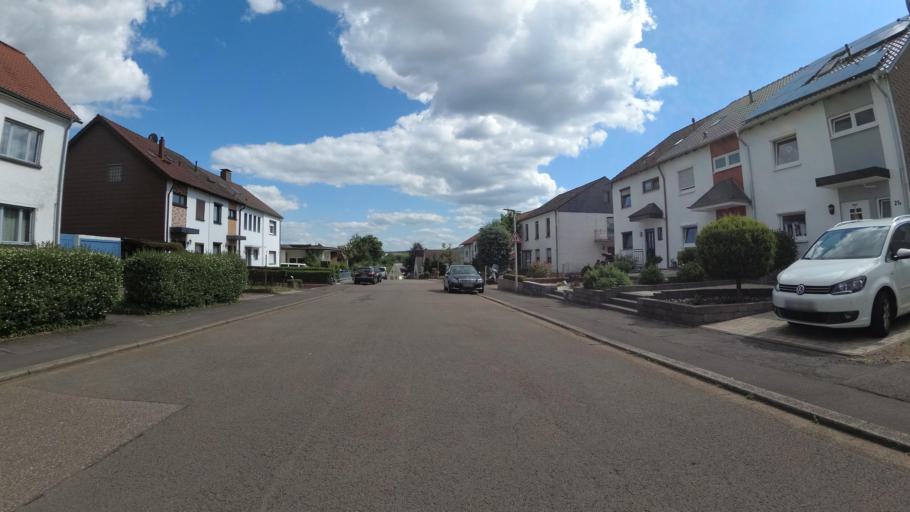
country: DE
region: Saarland
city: Volklingen
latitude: 49.2576
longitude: 6.8650
